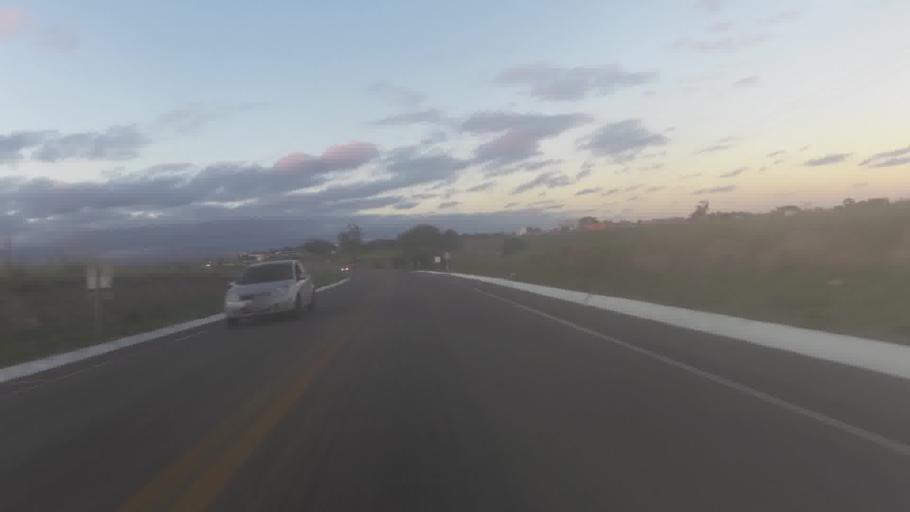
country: BR
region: Espirito Santo
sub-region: Marataizes
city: Marataizes
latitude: -21.0501
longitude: -40.8454
